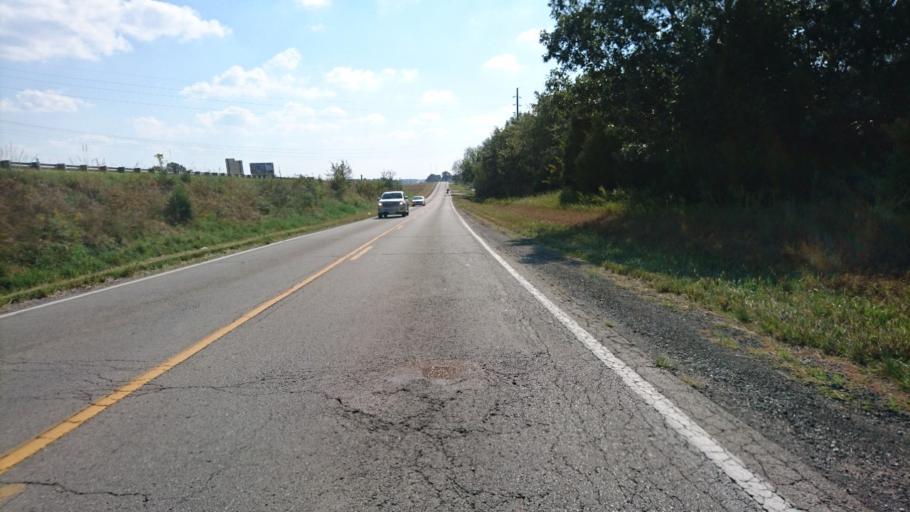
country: US
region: Missouri
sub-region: Laclede County
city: Lebanon
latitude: 37.6454
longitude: -92.6709
